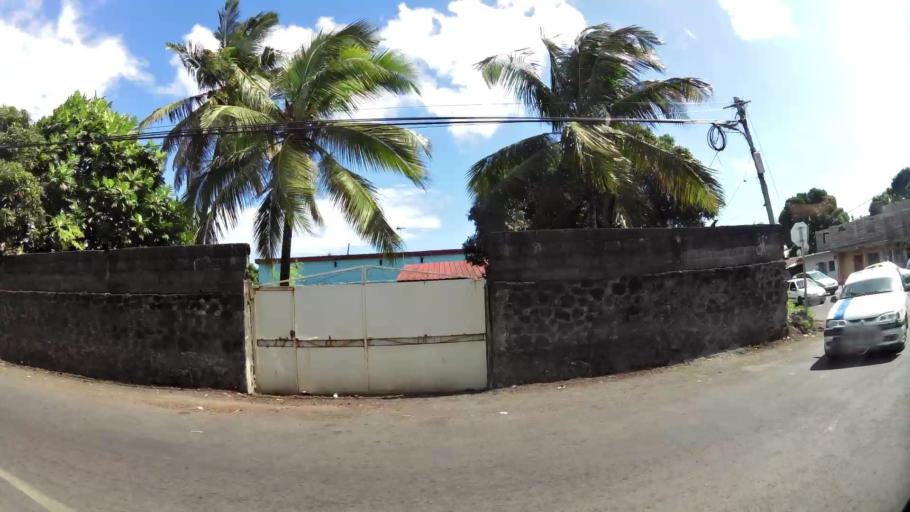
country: KM
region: Grande Comore
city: Mavingouni
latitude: -11.7205
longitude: 43.2506
